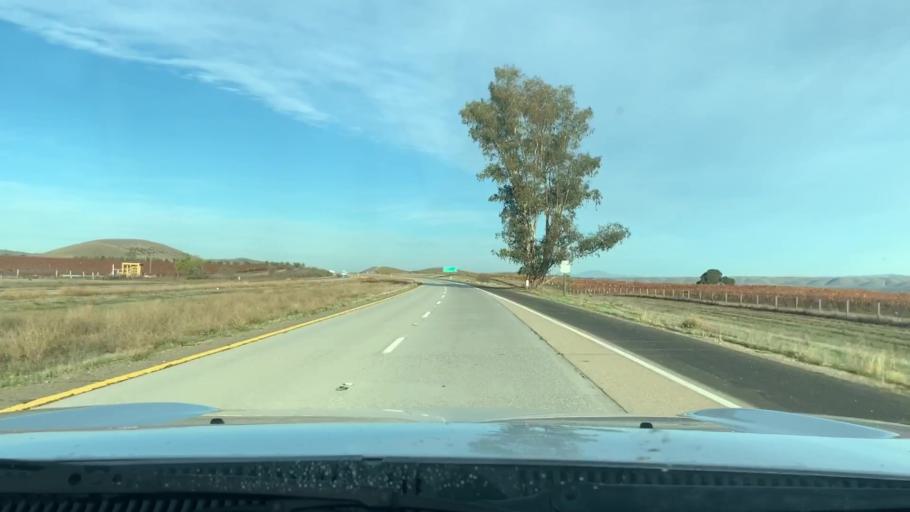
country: US
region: California
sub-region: Monterey County
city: King City
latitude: 36.0171
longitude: -120.9254
